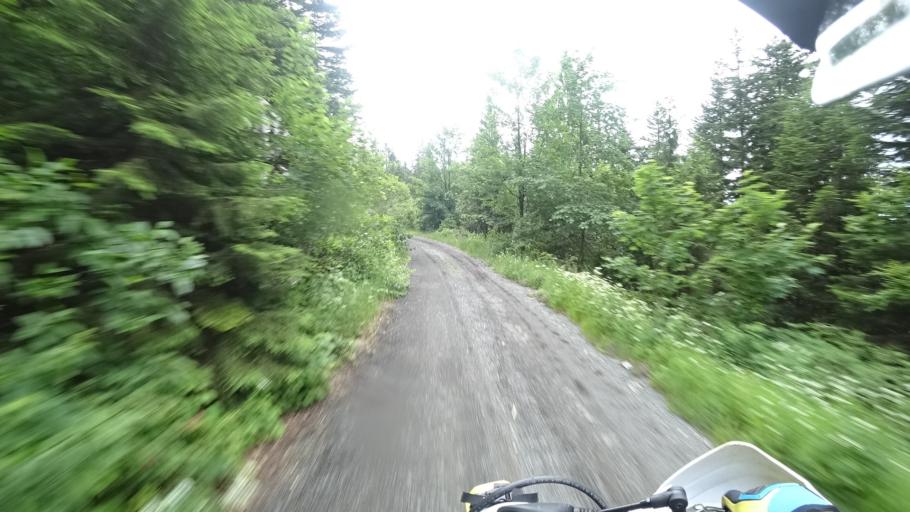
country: HR
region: Primorsko-Goranska
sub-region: Grad Delnice
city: Delnice
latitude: 45.3233
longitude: 14.7661
